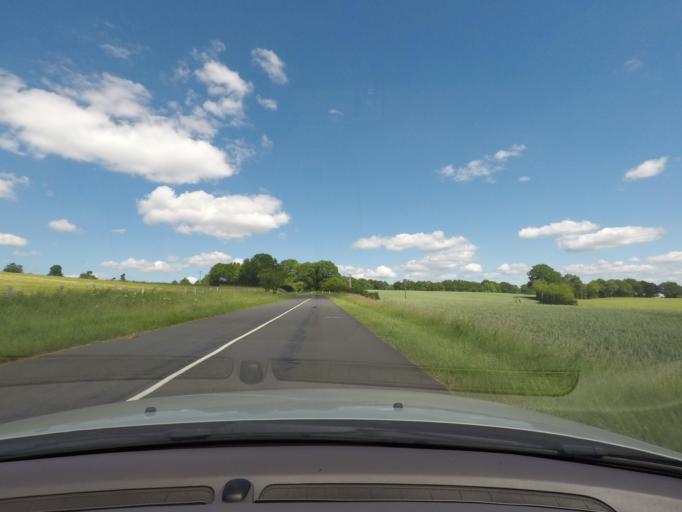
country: FR
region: Lower Normandy
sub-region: Departement de l'Orne
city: Mortagne-au-Perche
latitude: 48.5401
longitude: 0.5596
